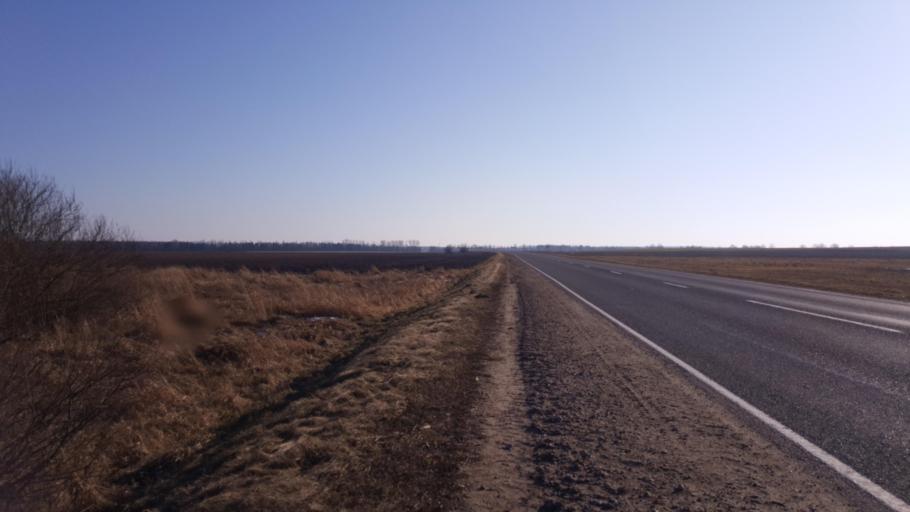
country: BY
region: Brest
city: Kamyanyets
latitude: 52.3852
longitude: 23.7877
